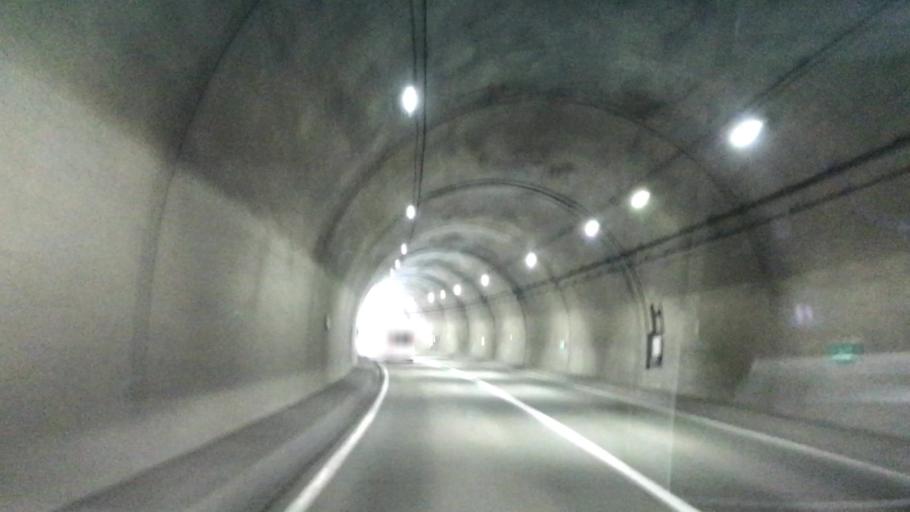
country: JP
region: Hokkaido
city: Shimo-furano
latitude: 42.9545
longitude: 142.6057
